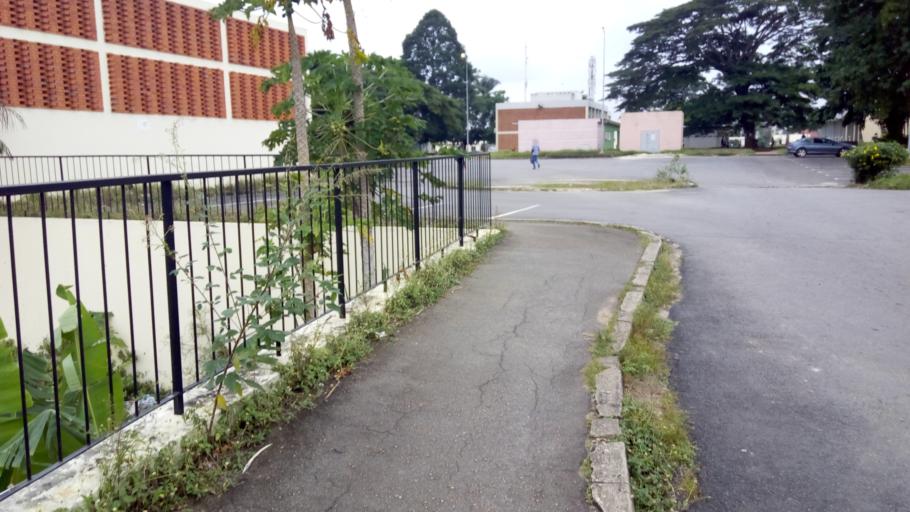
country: CI
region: Lagunes
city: Abidjan
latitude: 5.3429
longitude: -3.9856
